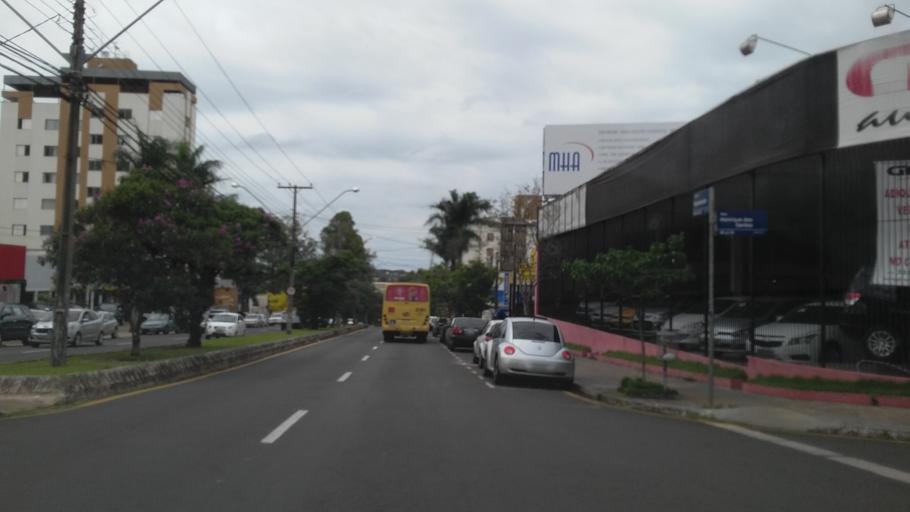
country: BR
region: Parana
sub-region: Londrina
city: Londrina
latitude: -23.3248
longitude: -51.1677
